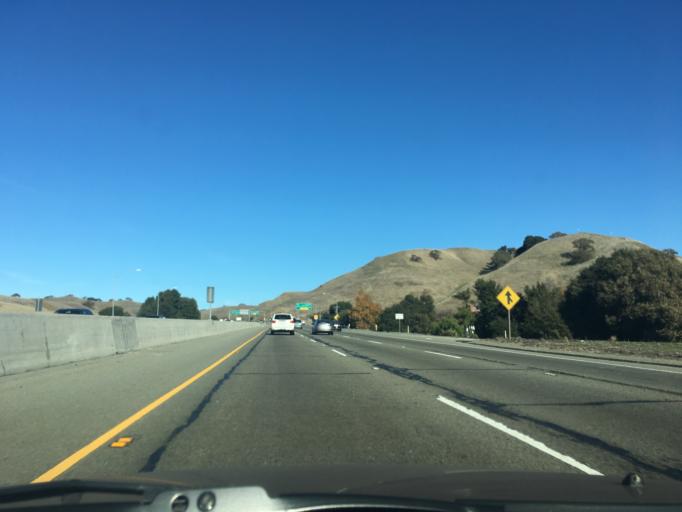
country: US
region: California
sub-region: Alameda County
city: Pleasanton
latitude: 37.5871
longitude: -121.8718
